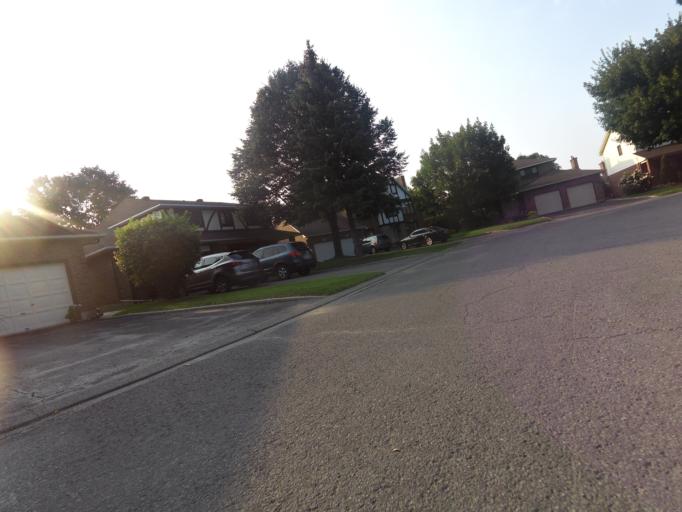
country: CA
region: Ontario
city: Bells Corners
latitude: 45.2887
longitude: -75.7475
